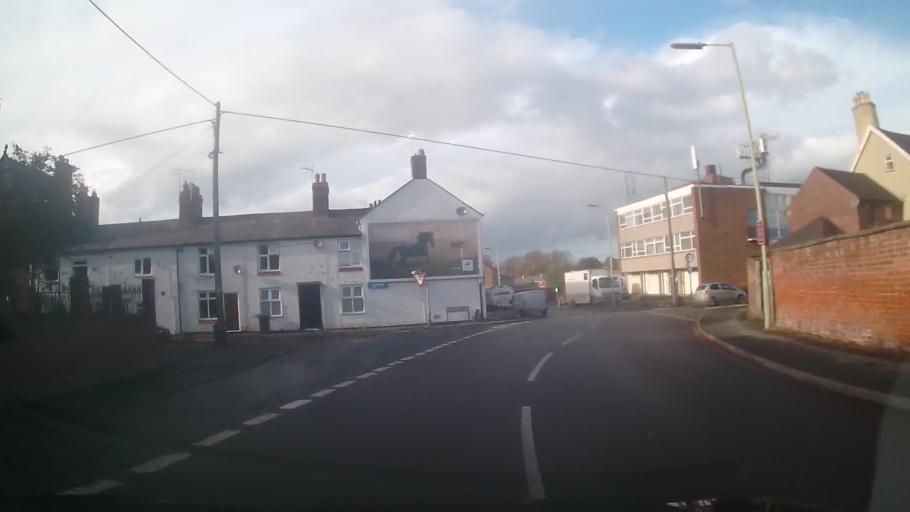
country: GB
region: England
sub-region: Shropshire
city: Whitchurch
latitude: 52.9662
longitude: -2.6835
